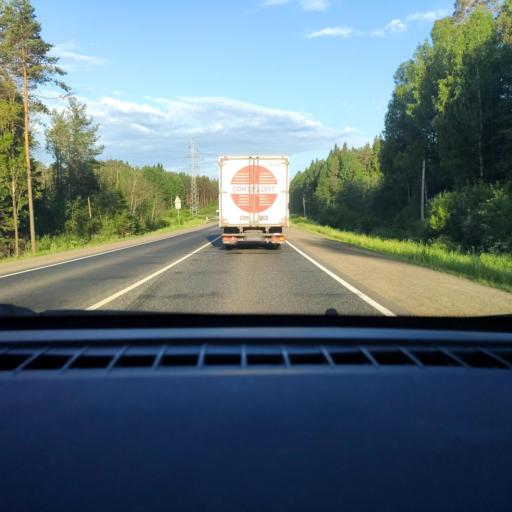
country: RU
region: Perm
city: Pavlovskiy
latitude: 57.8715
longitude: 54.8611
